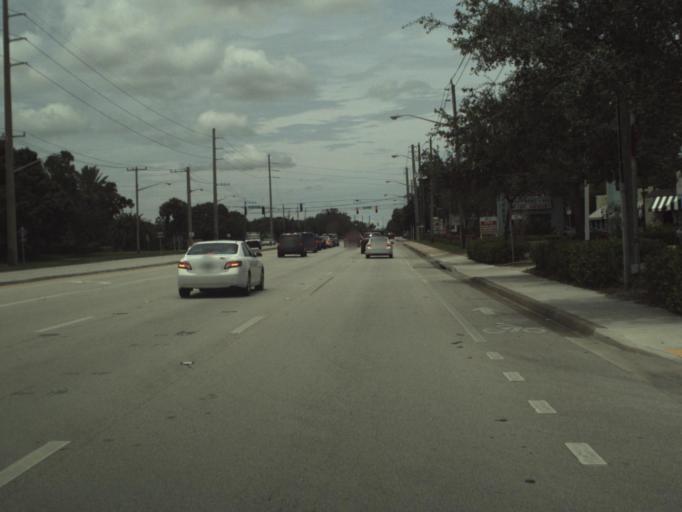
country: US
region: Florida
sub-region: Palm Beach County
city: Limestone Creek
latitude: 26.9343
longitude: -80.1232
